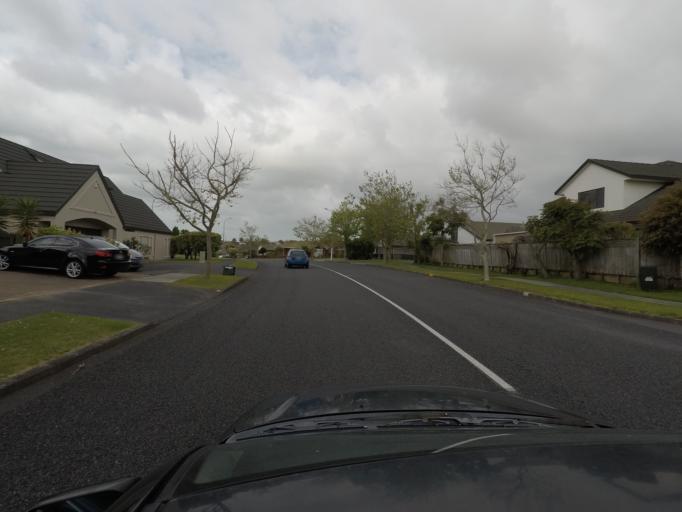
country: NZ
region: Auckland
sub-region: Auckland
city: Pakuranga
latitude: -36.9261
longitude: 174.9163
